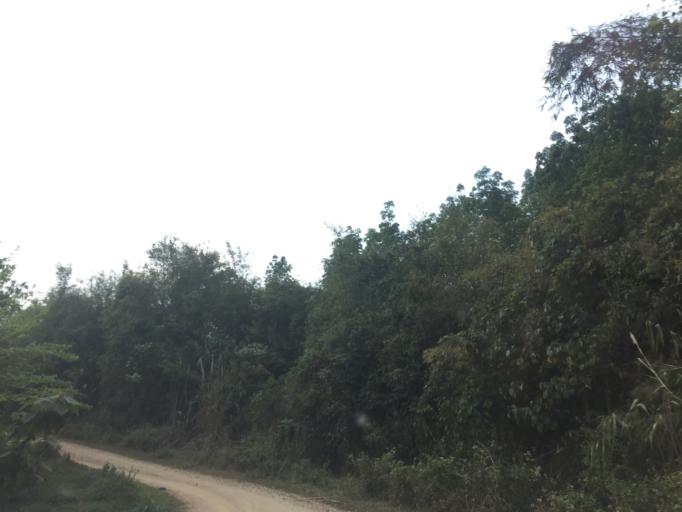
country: TH
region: Nan
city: Song Khwae
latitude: 19.7415
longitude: 100.7132
